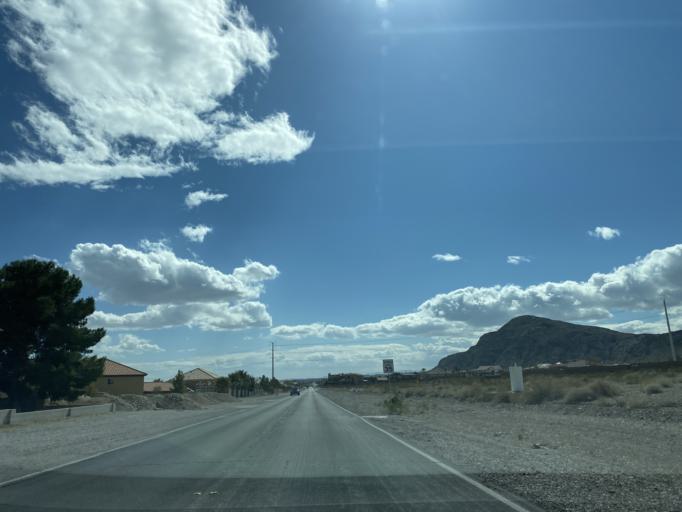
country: US
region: Nevada
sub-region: Clark County
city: Summerlin South
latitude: 36.2554
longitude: -115.3062
